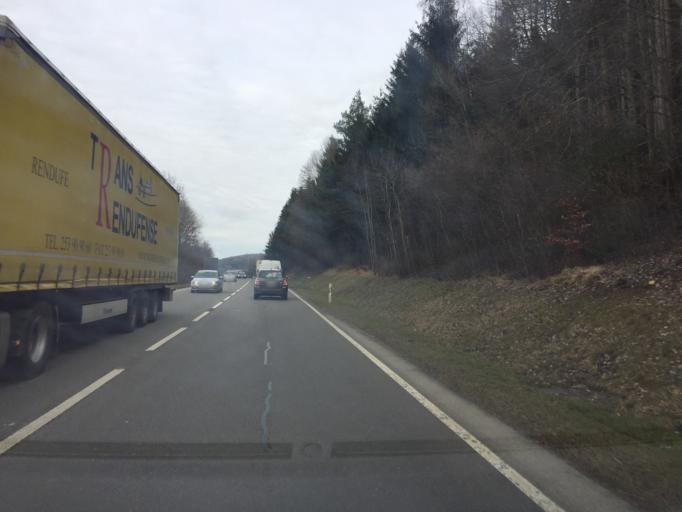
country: DE
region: Baden-Wuerttemberg
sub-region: Freiburg Region
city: Geisingen
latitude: 47.9167
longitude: 8.6567
